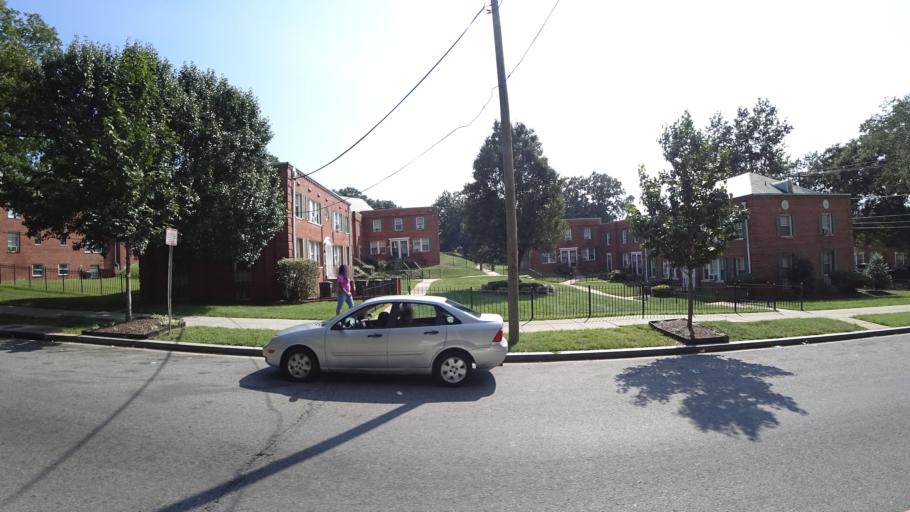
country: US
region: Maryland
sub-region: Prince George's County
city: Hillcrest Heights
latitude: 38.8620
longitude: -76.9704
